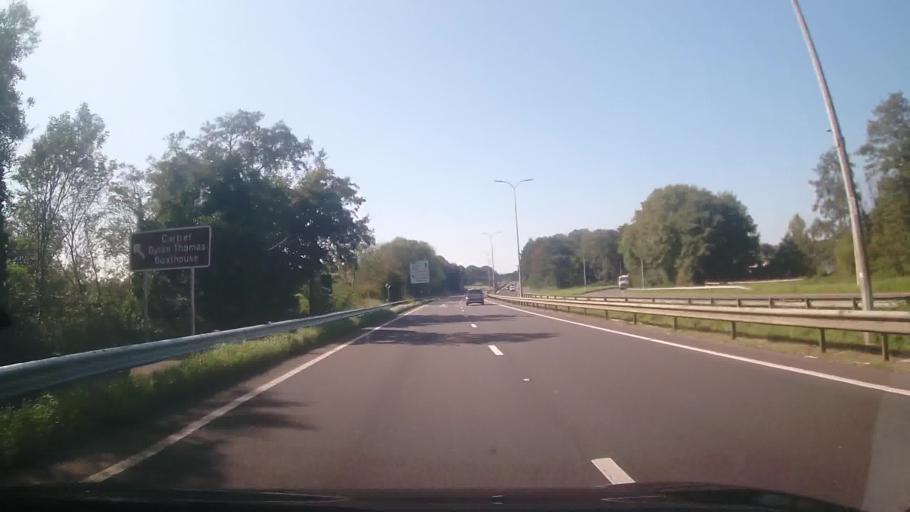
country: GB
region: Wales
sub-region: Carmarthenshire
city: Saint Clears
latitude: 51.8184
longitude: -4.4946
